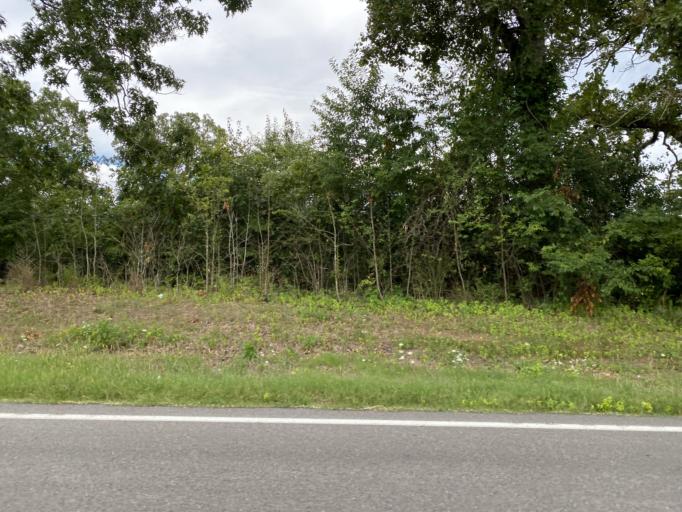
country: US
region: Arkansas
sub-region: Fulton County
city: Salem
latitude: 36.3601
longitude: -91.8335
